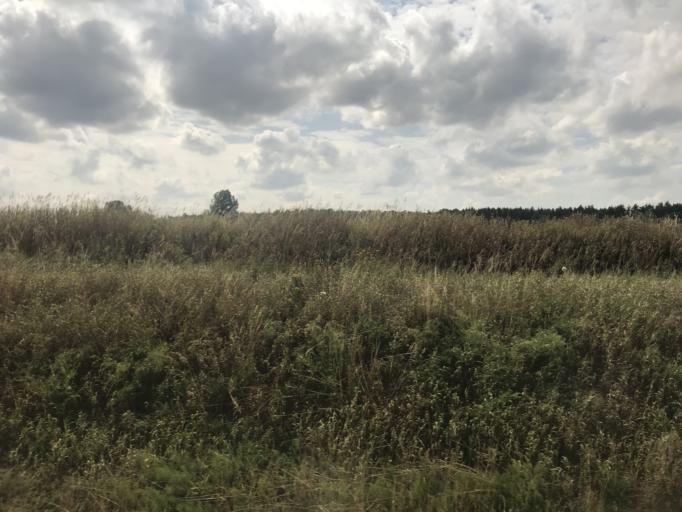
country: PL
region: Greater Poland Voivodeship
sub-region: Powiat gnieznienski
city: Lubowo
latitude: 52.4921
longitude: 17.3717
